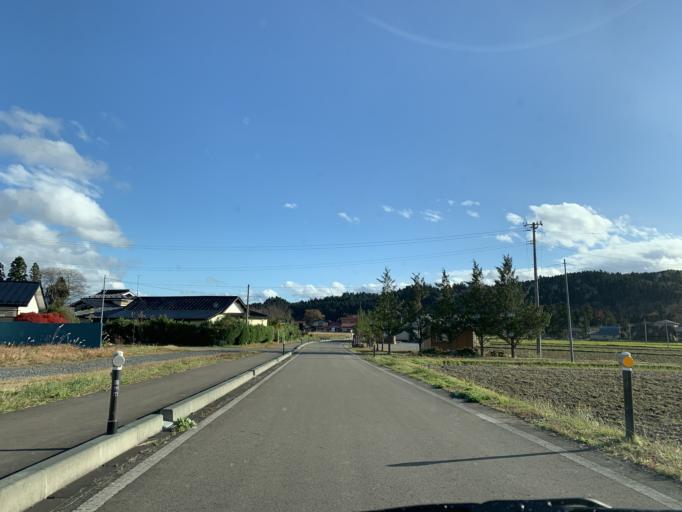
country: JP
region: Iwate
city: Ichinoseki
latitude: 39.0119
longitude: 141.0959
